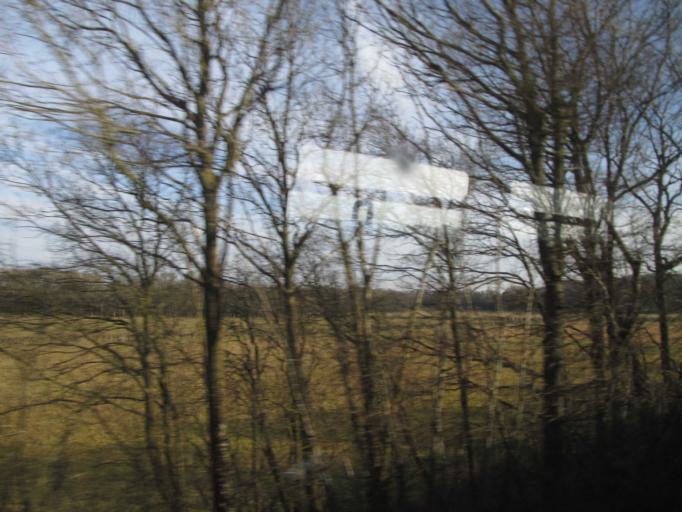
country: GB
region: England
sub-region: Surrey
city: Normandy
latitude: 51.2441
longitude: -0.6753
